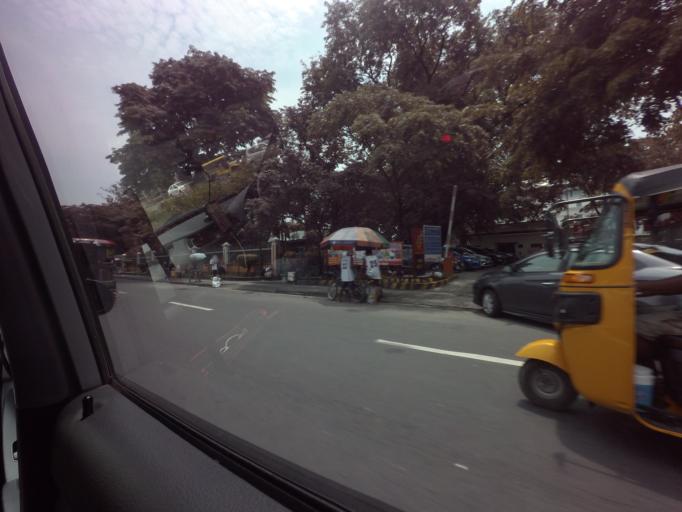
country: PH
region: Metro Manila
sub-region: City of Manila
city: Port Area
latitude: 14.5826
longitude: 120.9809
